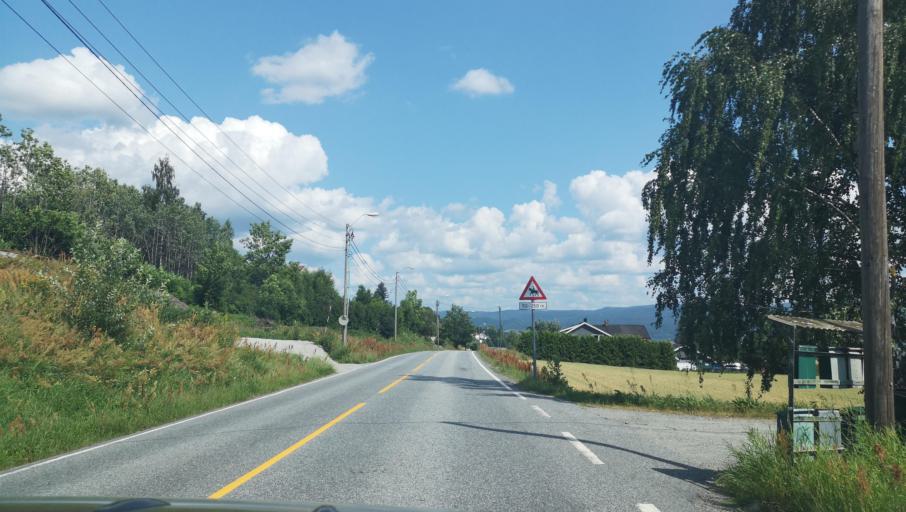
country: NO
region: Buskerud
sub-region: Ovre Eiker
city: Hokksund
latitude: 59.7314
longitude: 9.8462
